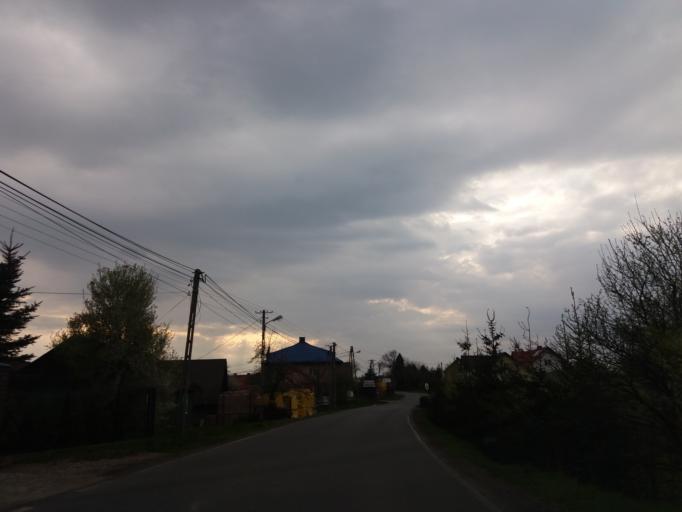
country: PL
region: Lesser Poland Voivodeship
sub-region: Powiat krakowski
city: Rzeszotary
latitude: 49.9269
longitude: 20.0154
